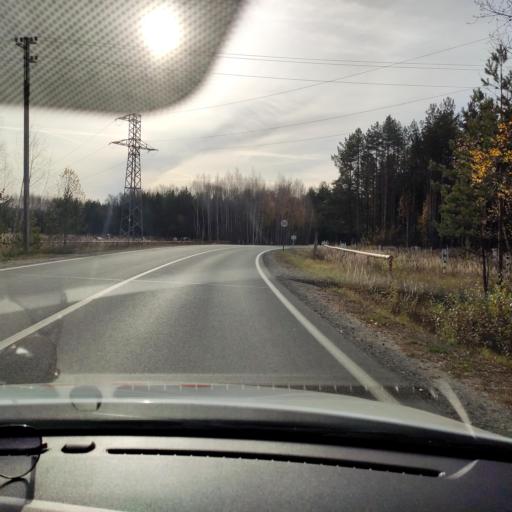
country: RU
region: Tatarstan
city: Verkhniy Uslon
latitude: 55.6370
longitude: 49.0222
